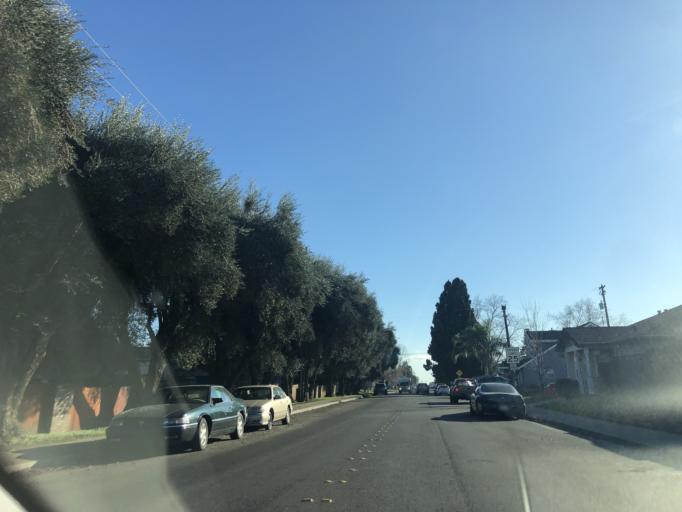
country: US
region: California
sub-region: Yolo County
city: Woodland
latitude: 38.6673
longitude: -121.7471
